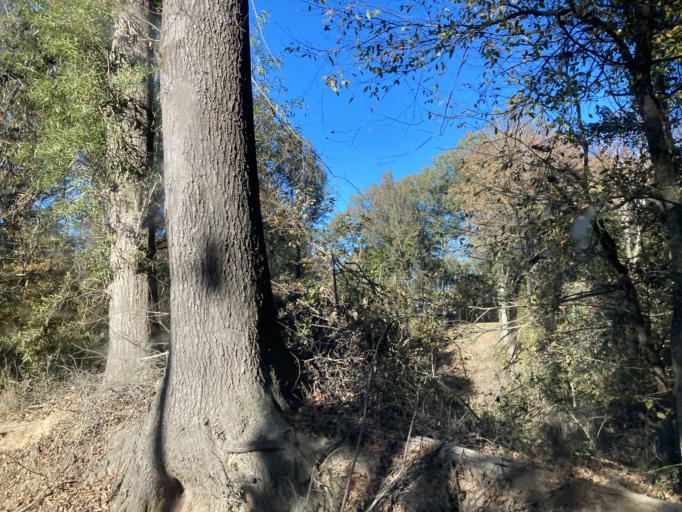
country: US
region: Mississippi
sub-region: Yazoo County
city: Yazoo City
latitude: 32.7380
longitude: -90.4389
